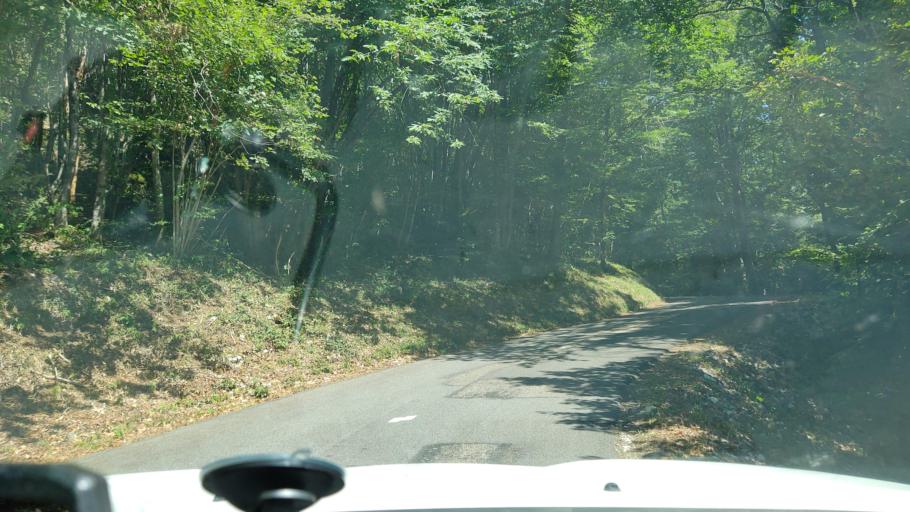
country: FR
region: Rhone-Alpes
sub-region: Departement de la Savoie
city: Le Bourget-du-Lac
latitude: 45.6558
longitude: 5.8431
